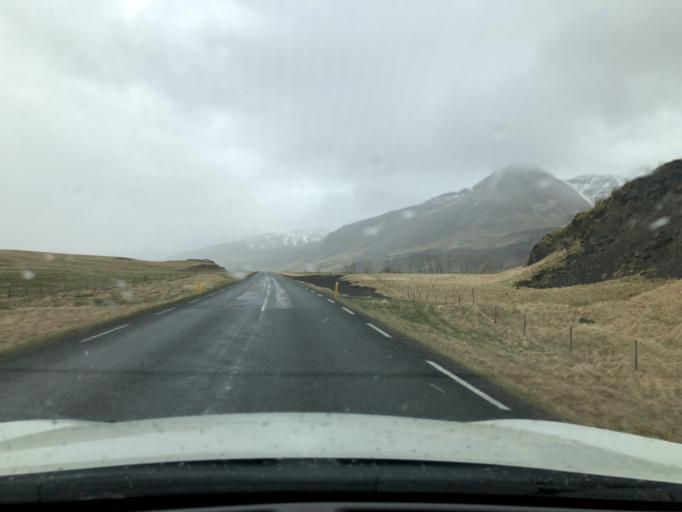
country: IS
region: East
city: Hoefn
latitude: 64.3448
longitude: -15.2469
